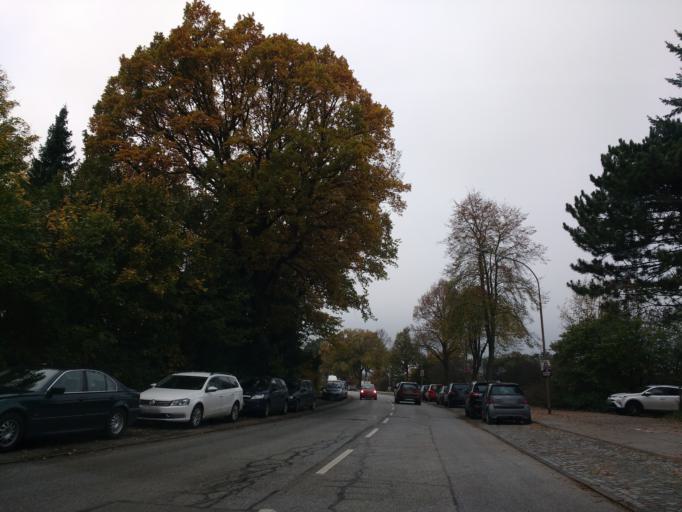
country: DE
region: Schleswig-Holstein
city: Luebeck
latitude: 53.8713
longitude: 10.7360
